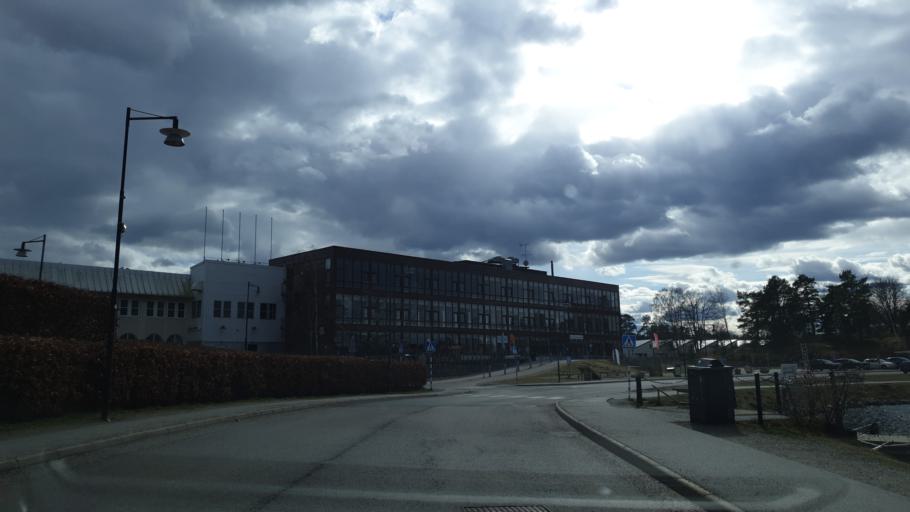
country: SE
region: Stockholm
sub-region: Varmdo Kommun
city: Gustavsberg
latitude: 59.3239
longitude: 18.3811
